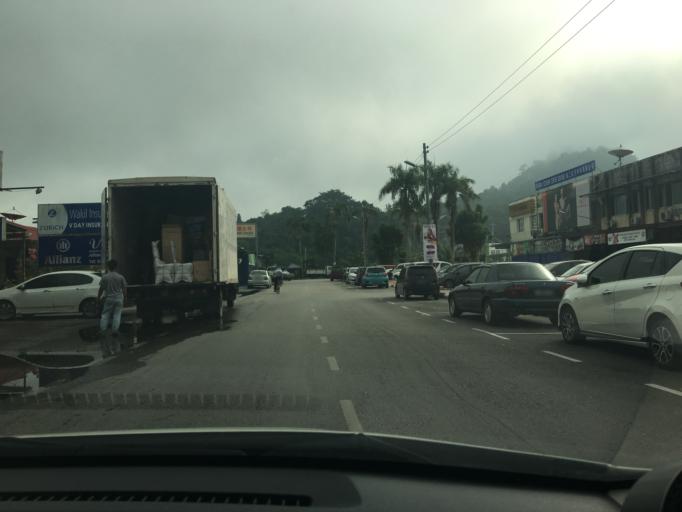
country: MY
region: Sarawak
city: Kuching
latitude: 1.4185
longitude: 110.1547
